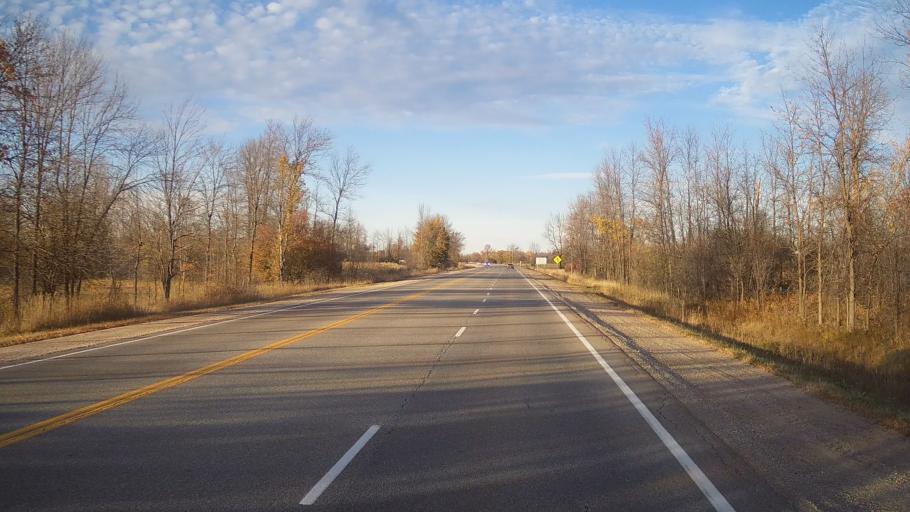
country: CA
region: Ontario
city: Perth
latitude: 44.9732
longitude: -76.2279
